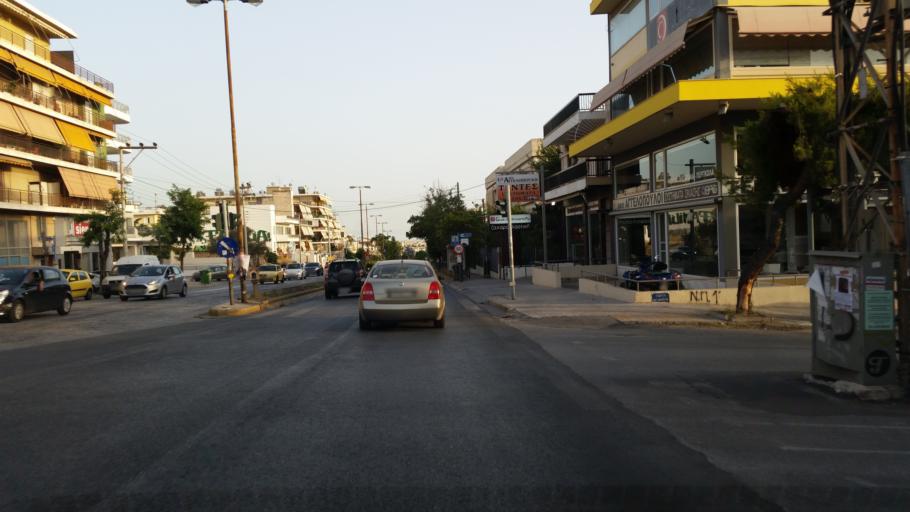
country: GR
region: Attica
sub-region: Nomarchia Athinas
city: Argyroupoli
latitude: 37.9115
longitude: 23.7544
